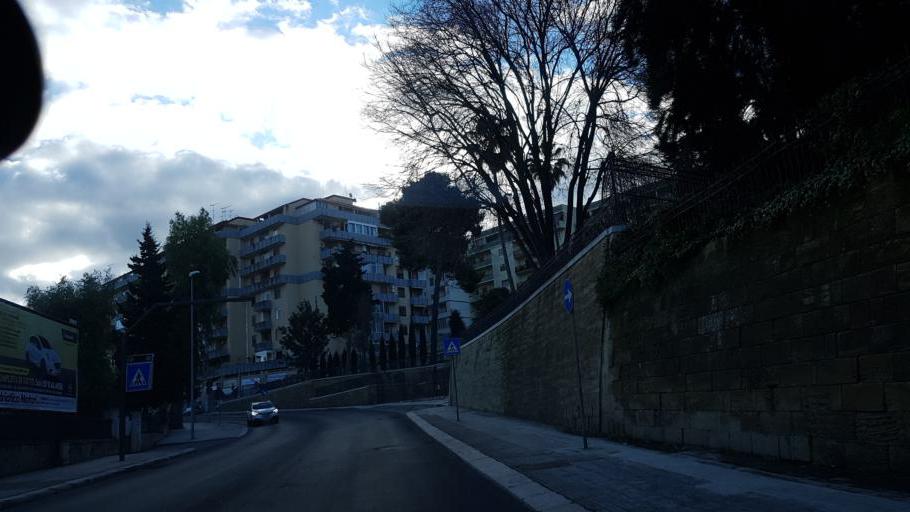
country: IT
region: Apulia
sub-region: Provincia di Brindisi
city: Brindisi
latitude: 40.6383
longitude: 17.9279
